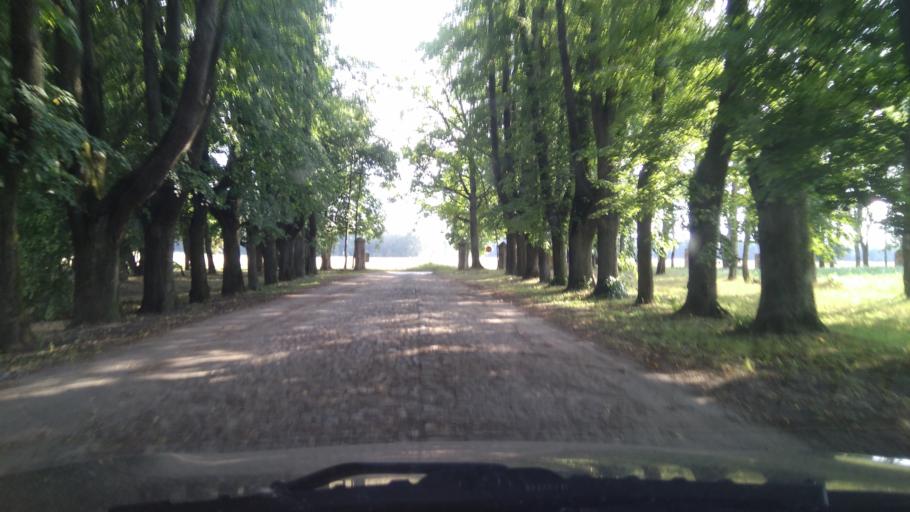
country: BY
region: Brest
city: Lyakhavichy
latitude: 53.0233
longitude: 26.3395
